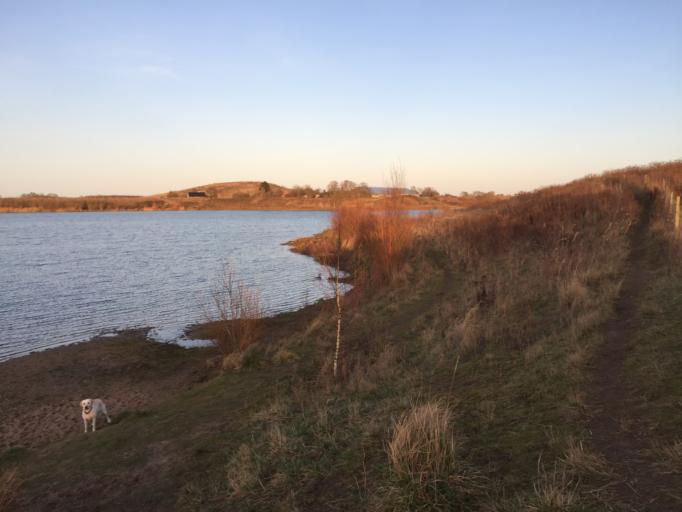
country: DK
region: South Denmark
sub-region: Kerteminde Kommune
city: Langeskov
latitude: 55.3277
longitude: 10.5282
